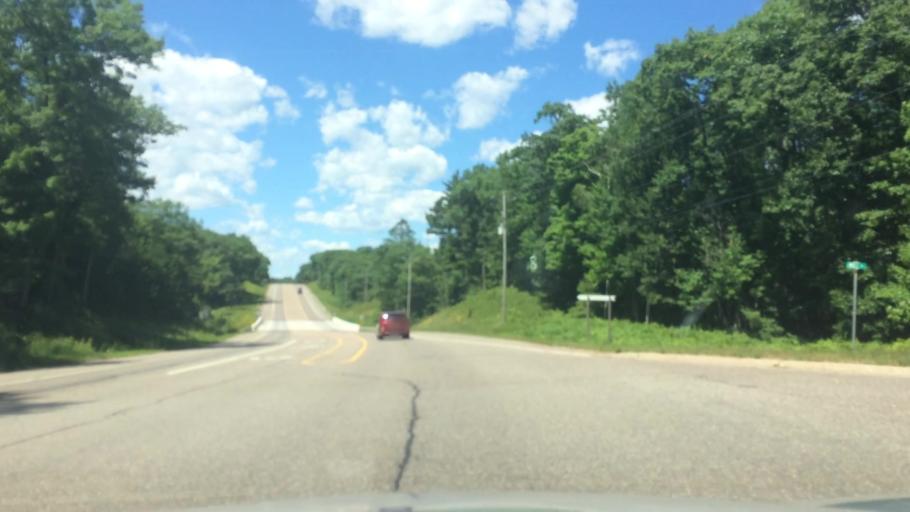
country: US
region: Wisconsin
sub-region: Vilas County
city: Lac du Flambeau
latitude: 45.7901
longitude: -89.7108
